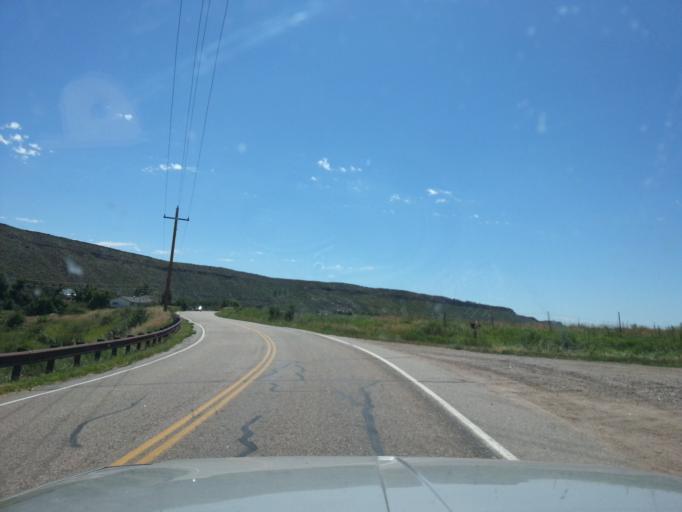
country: US
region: Colorado
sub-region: Larimer County
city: Loveland
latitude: 40.4692
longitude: -105.2104
